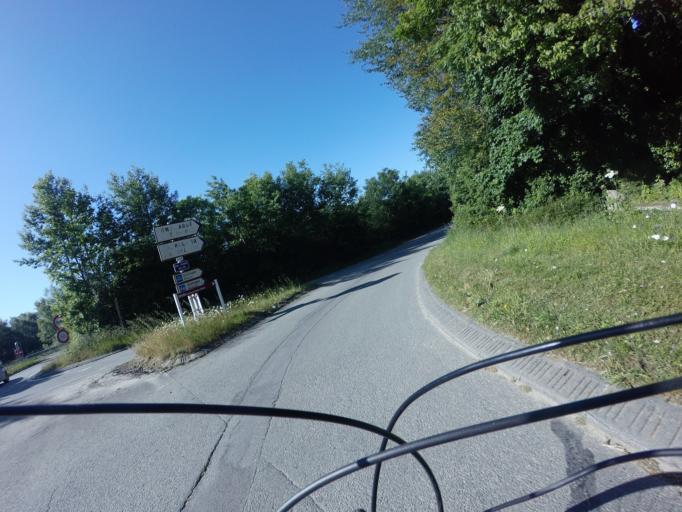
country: FR
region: Brittany
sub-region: Departement du Finistere
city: Plomelin
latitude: 47.9679
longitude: -4.1452
